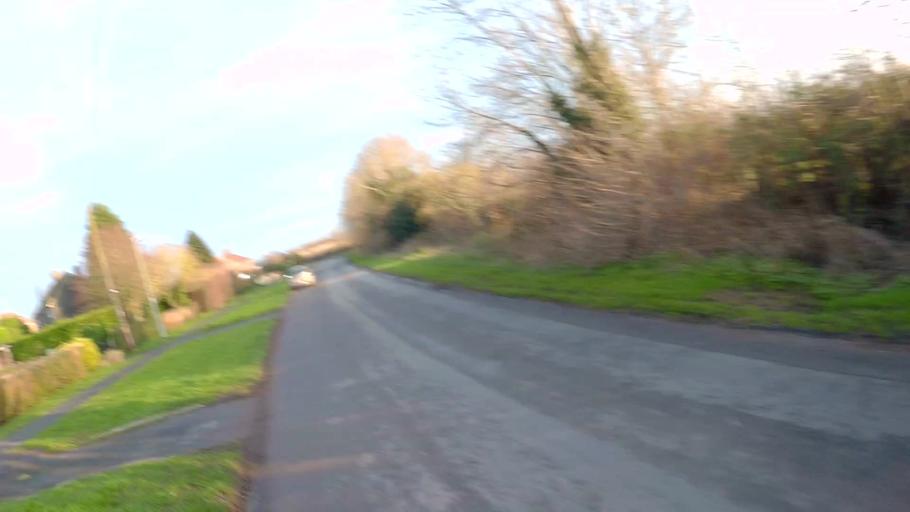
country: GB
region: England
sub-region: Lincolnshire
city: Bourne
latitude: 52.8021
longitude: -0.3867
